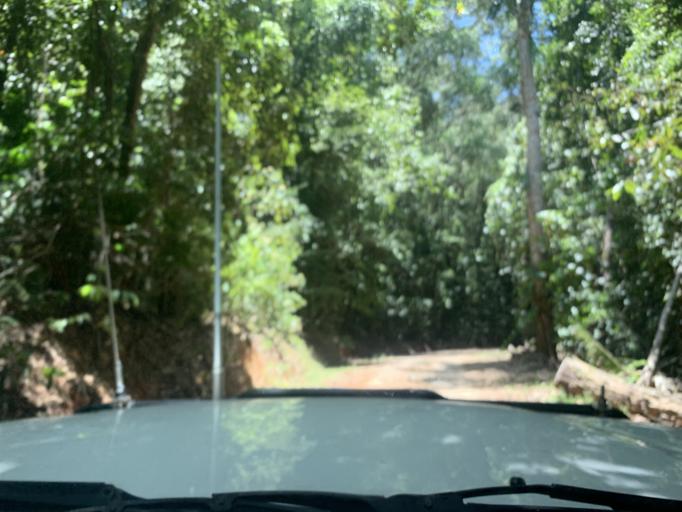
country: AU
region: Queensland
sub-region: Cairns
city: Redlynch
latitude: -16.9444
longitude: 145.6307
